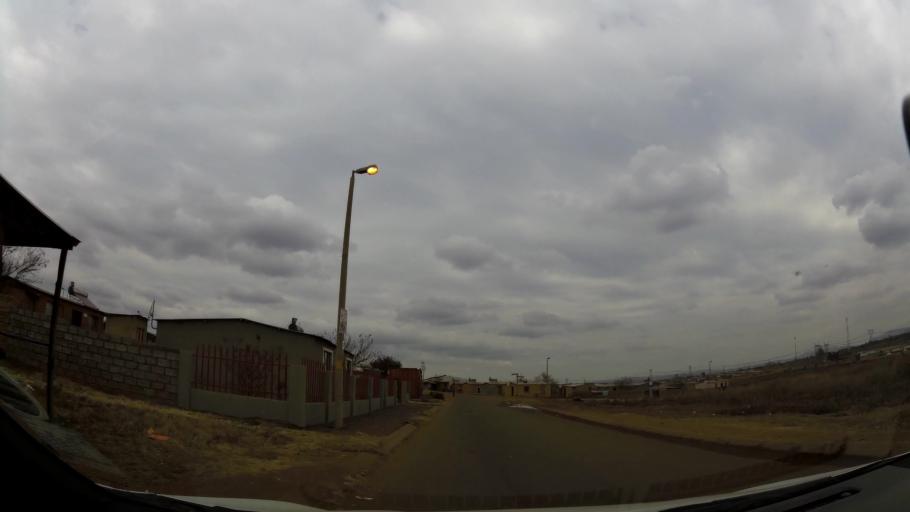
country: ZA
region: Gauteng
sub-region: Ekurhuleni Metropolitan Municipality
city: Germiston
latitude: -26.3759
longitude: 28.1174
